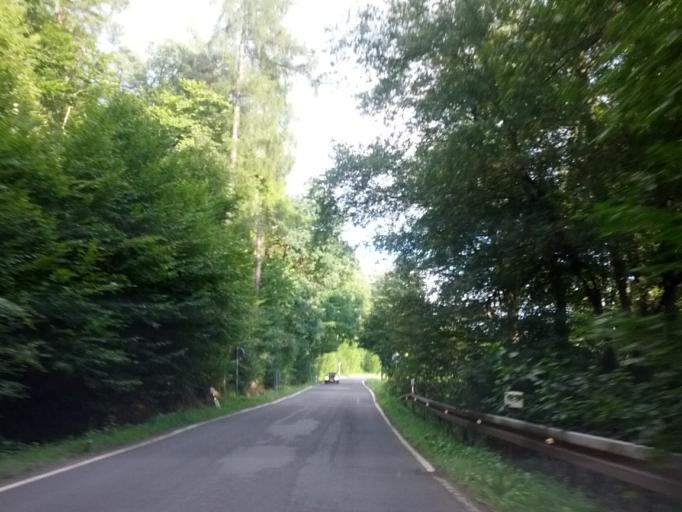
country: DE
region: Thuringia
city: Wolfsburg-Unkeroda
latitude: 50.9309
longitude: 10.2795
